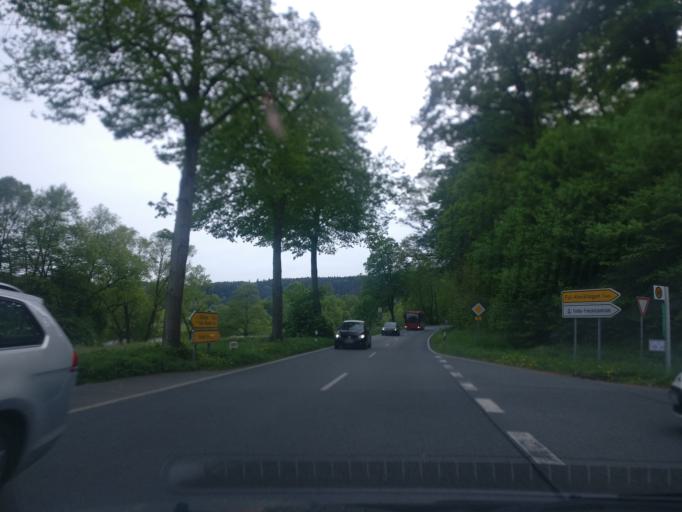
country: DE
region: Hesse
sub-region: Regierungsbezirk Kassel
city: Fuldatal
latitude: 51.3891
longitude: 9.5639
